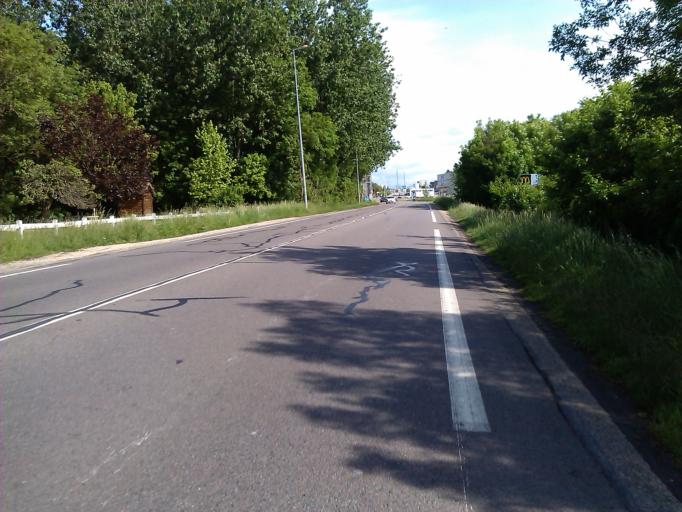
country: FR
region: Bourgogne
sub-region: Departement de Saone-et-Loire
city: Saint-Remy
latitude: 46.7617
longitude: 4.8425
